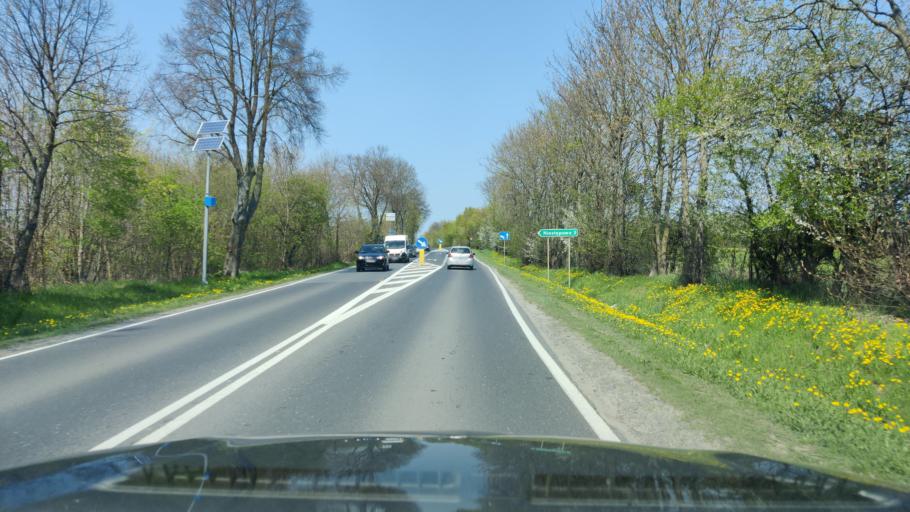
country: PL
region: Masovian Voivodeship
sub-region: Powiat pultuski
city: Pultusk
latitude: 52.6423
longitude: 21.0924
